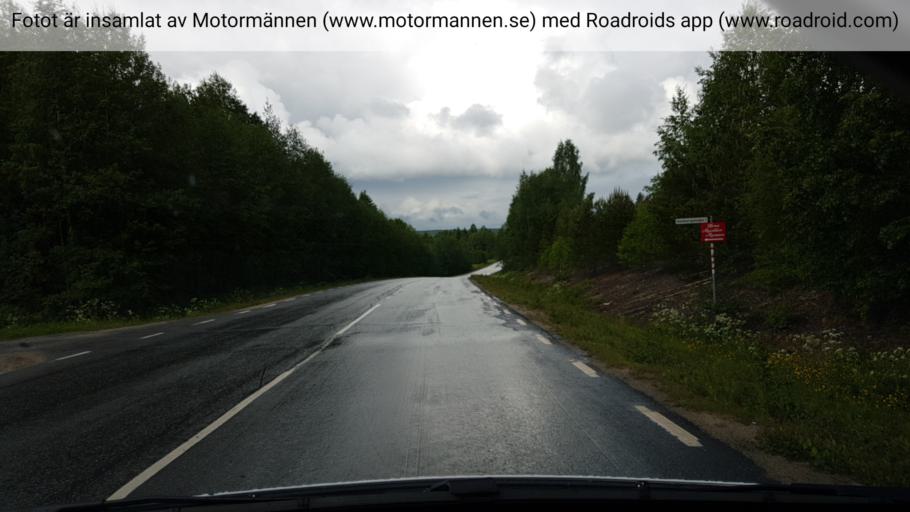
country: SE
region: Vaesterbotten
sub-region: Vannas Kommun
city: Vannasby
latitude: 63.9206
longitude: 19.7982
